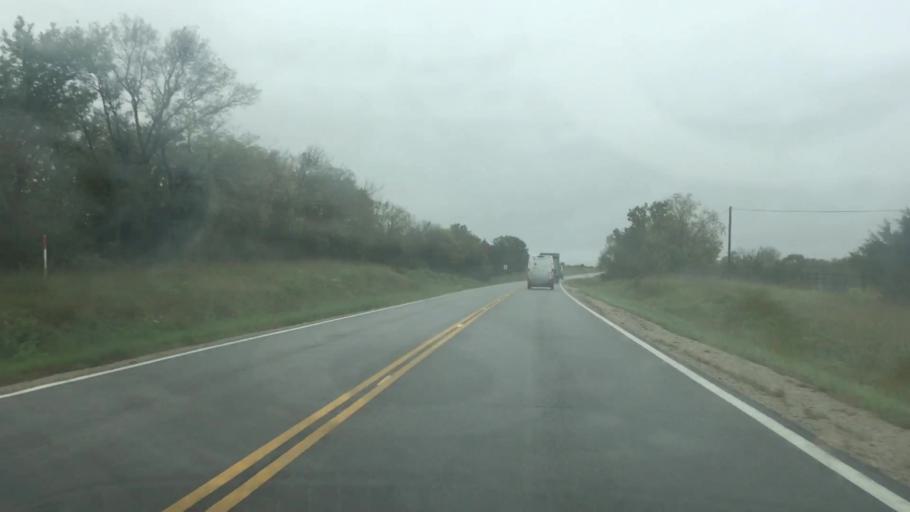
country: US
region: Kansas
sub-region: Anderson County
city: Garnett
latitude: 38.2020
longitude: -95.2495
